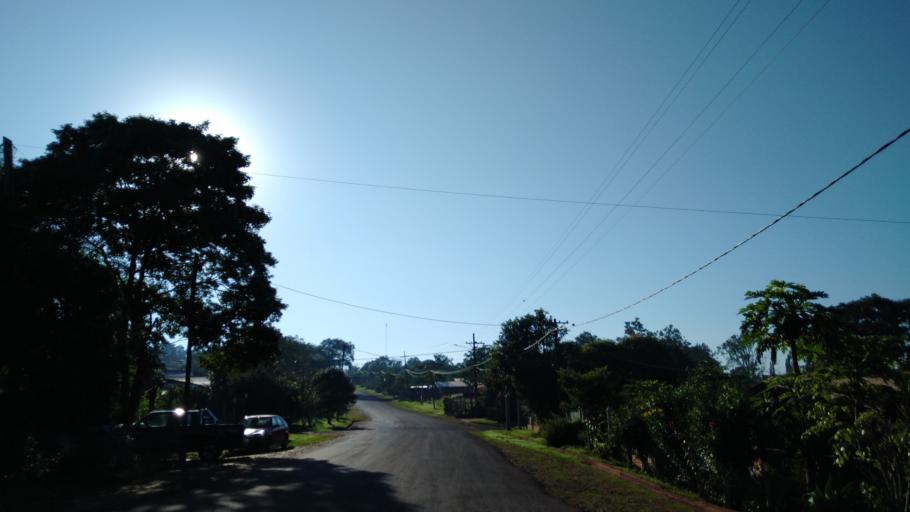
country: AR
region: Misiones
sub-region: Departamento de Montecarlo
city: Montecarlo
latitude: -26.5696
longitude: -54.7708
